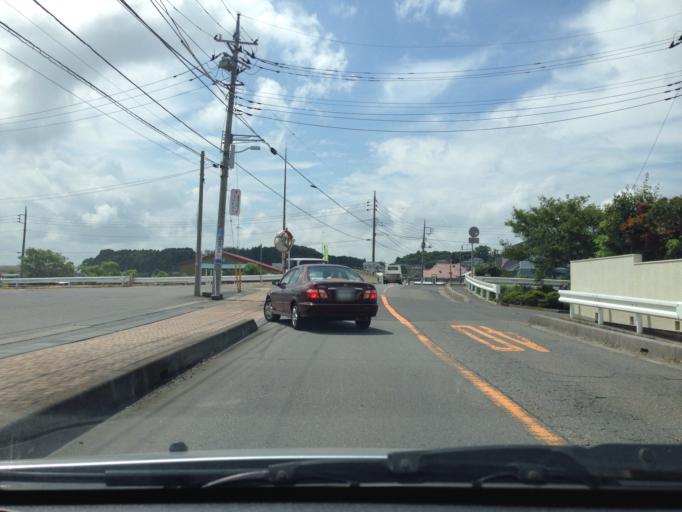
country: JP
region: Ibaraki
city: Ami
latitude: 36.0689
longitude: 140.2111
